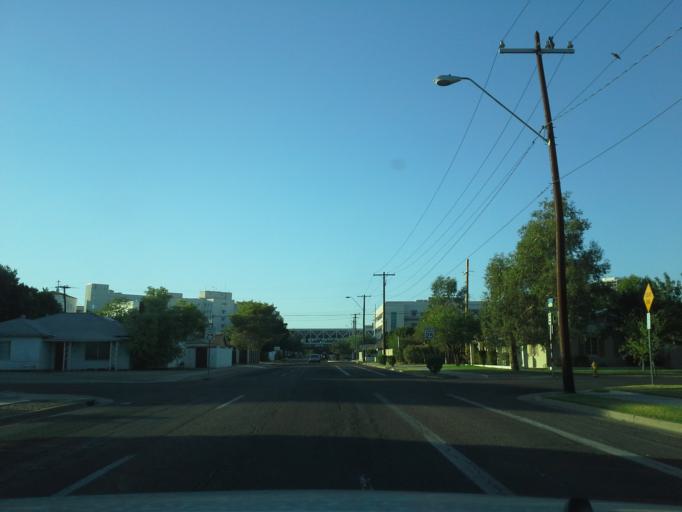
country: US
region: Arizona
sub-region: Maricopa County
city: Phoenix
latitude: 33.4783
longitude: -112.0782
